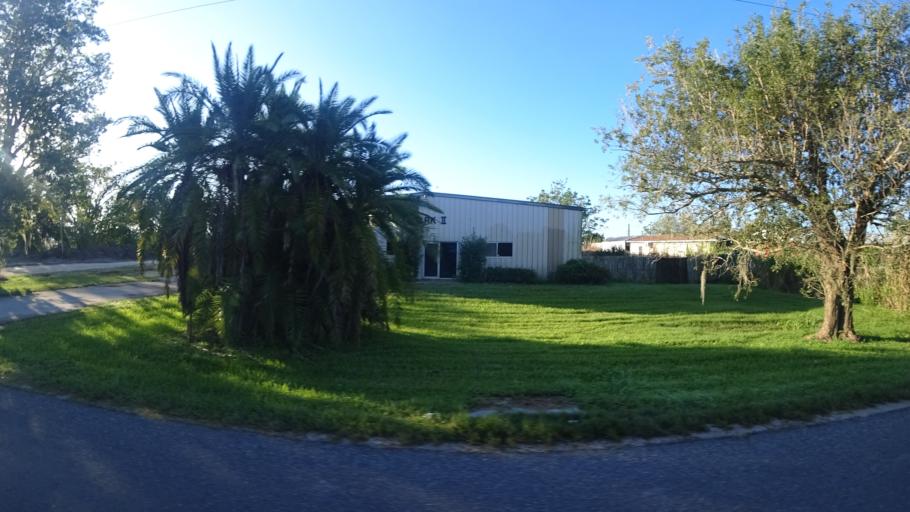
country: US
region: Florida
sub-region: Manatee County
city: Ellenton
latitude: 27.5327
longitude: -82.5340
